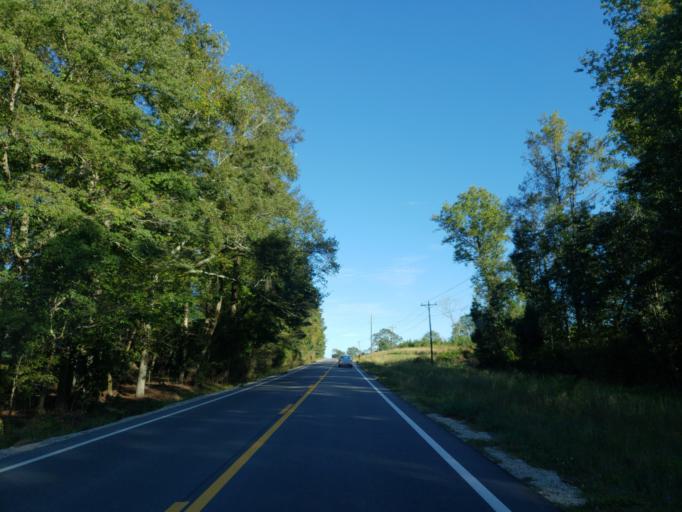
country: US
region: Mississippi
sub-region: Perry County
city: Richton
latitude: 31.3610
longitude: -89.0424
